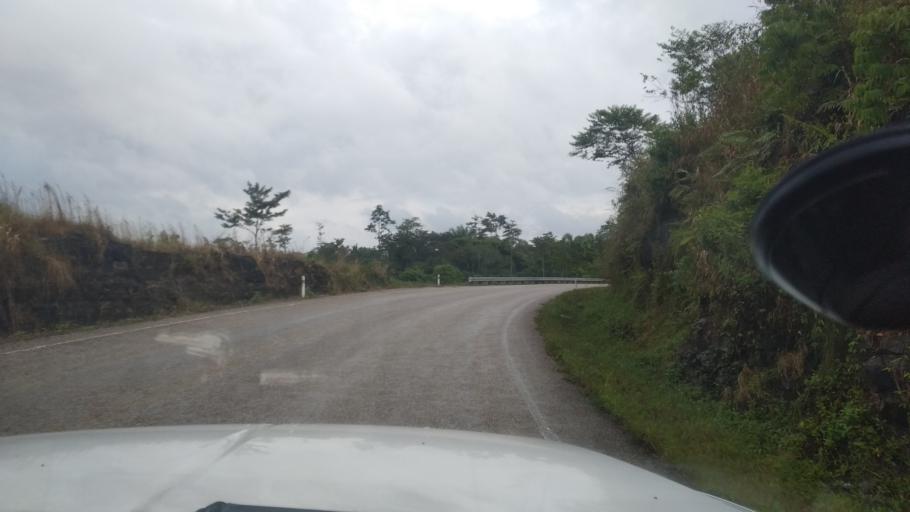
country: GT
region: Peten
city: San Luis
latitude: 16.1980
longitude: -89.1584
